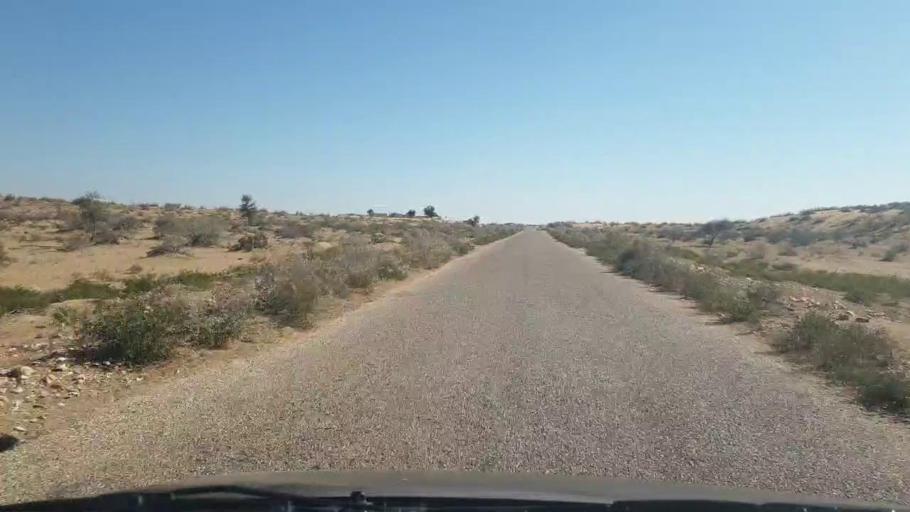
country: PK
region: Sindh
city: Bozdar
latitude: 27.0157
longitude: 68.7815
